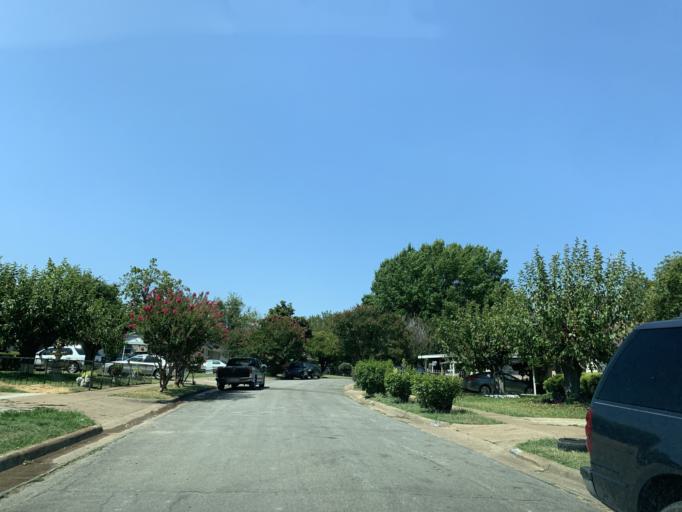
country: US
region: Texas
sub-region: Dallas County
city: Hutchins
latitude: 32.6741
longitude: -96.7531
